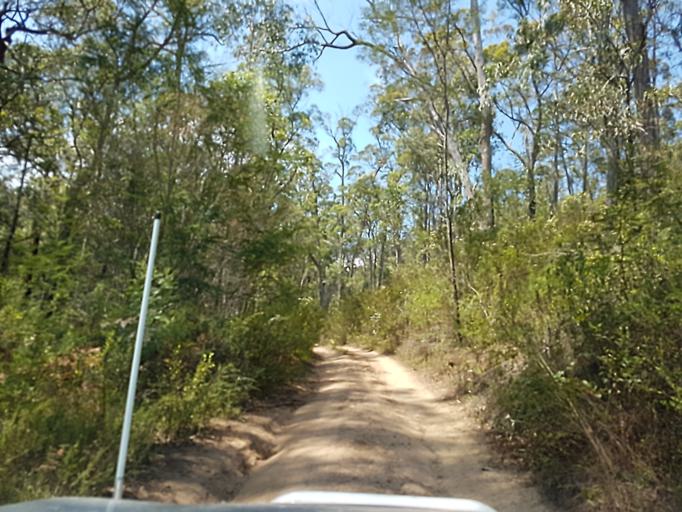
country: AU
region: Victoria
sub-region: East Gippsland
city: Lakes Entrance
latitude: -37.4048
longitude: 148.3147
